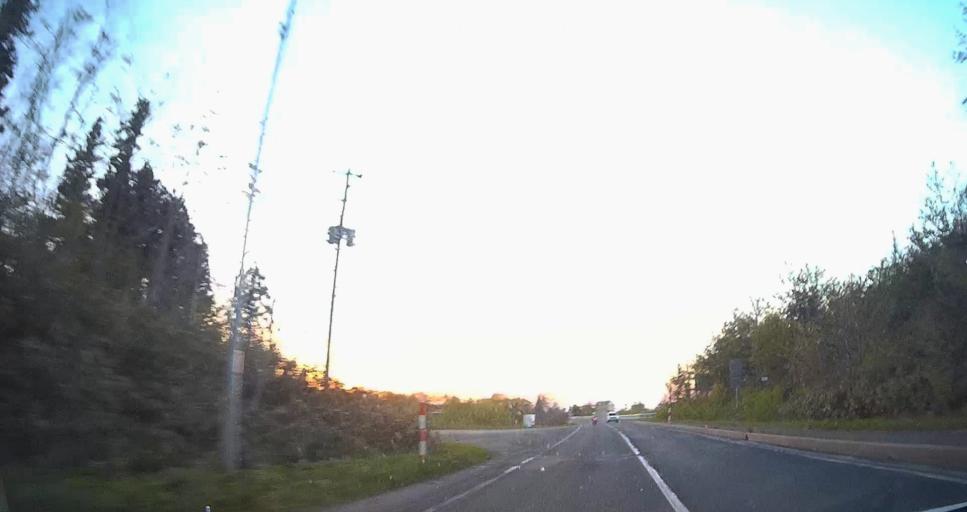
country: JP
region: Aomori
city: Misawa
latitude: 40.8665
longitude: 141.1097
